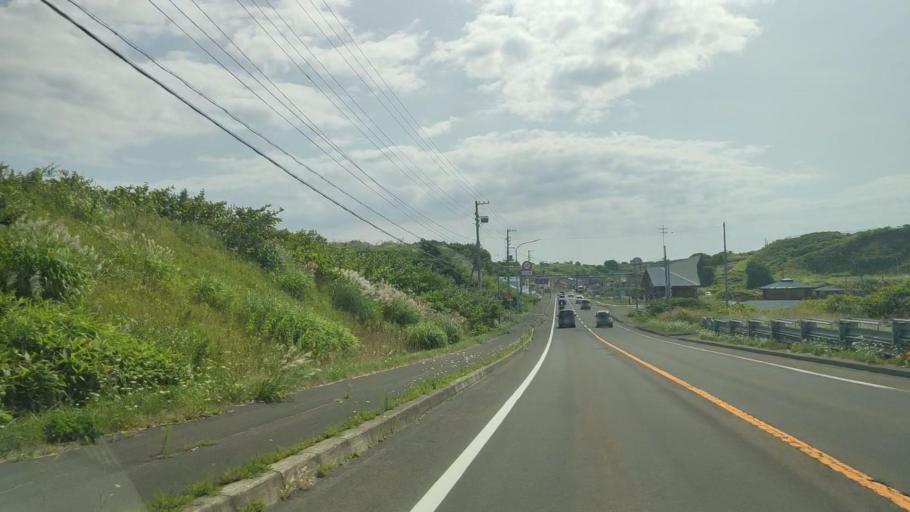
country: JP
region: Hokkaido
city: Rumoi
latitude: 44.3163
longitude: 141.6639
